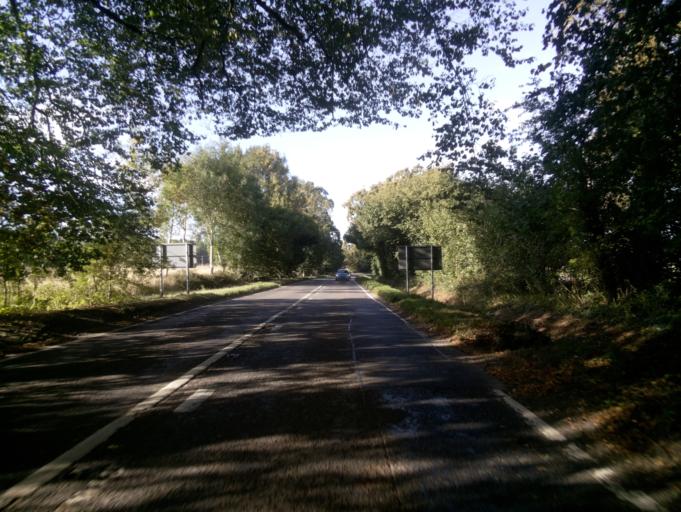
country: GB
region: England
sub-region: Hampshire
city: Alton
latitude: 51.1152
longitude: -0.9955
